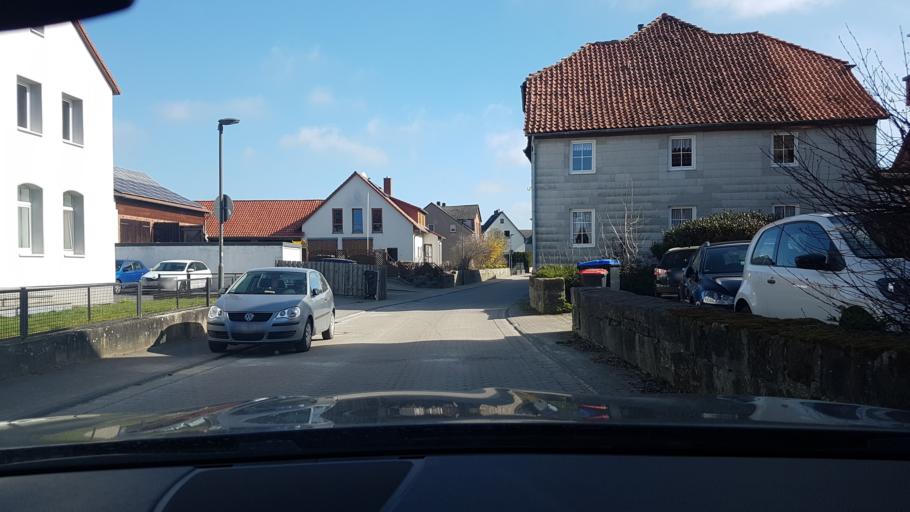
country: DE
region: Lower Saxony
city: Bad Munder am Deister
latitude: 52.1253
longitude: 9.4379
